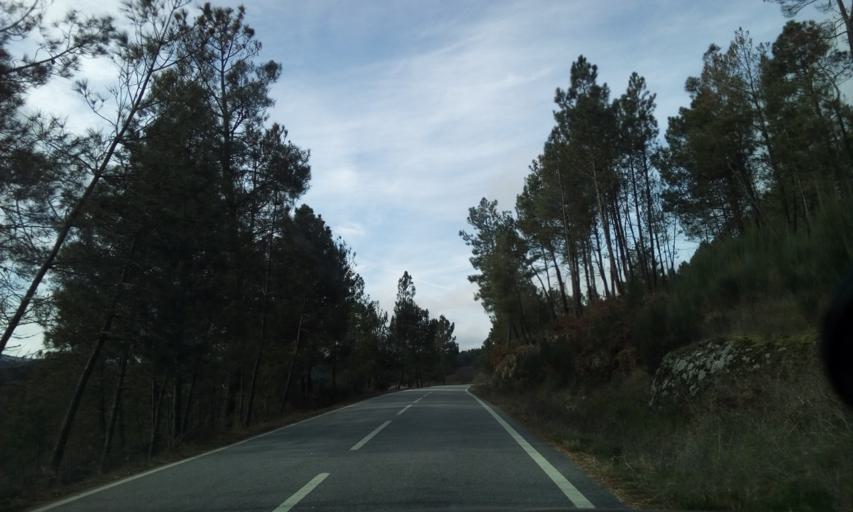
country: PT
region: Guarda
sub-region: Fornos de Algodres
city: Fornos de Algodres
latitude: 40.7167
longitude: -7.5599
